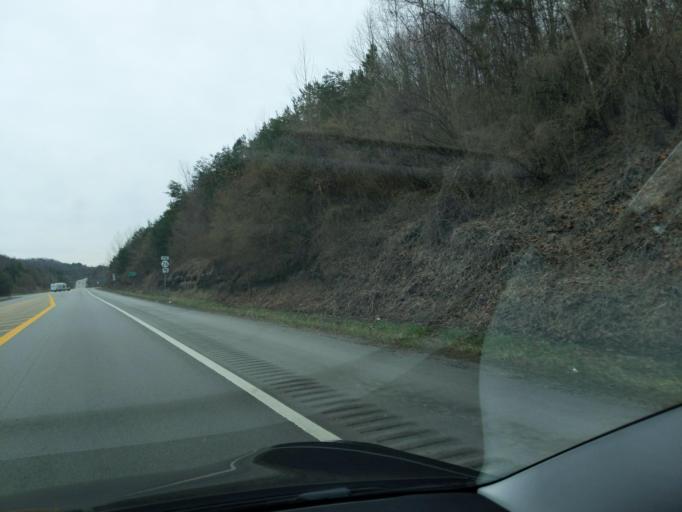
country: US
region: Kentucky
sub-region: Whitley County
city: Corbin
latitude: 36.9169
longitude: -84.0926
